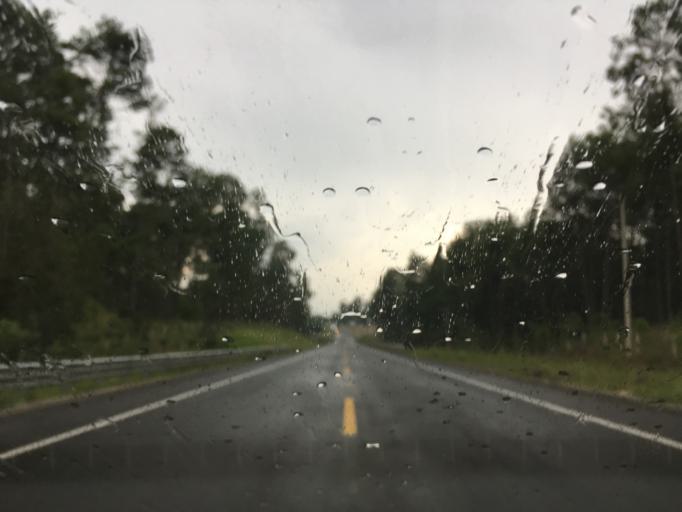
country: MX
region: Michoacan
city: Angahuan
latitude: 19.5217
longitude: -102.1818
